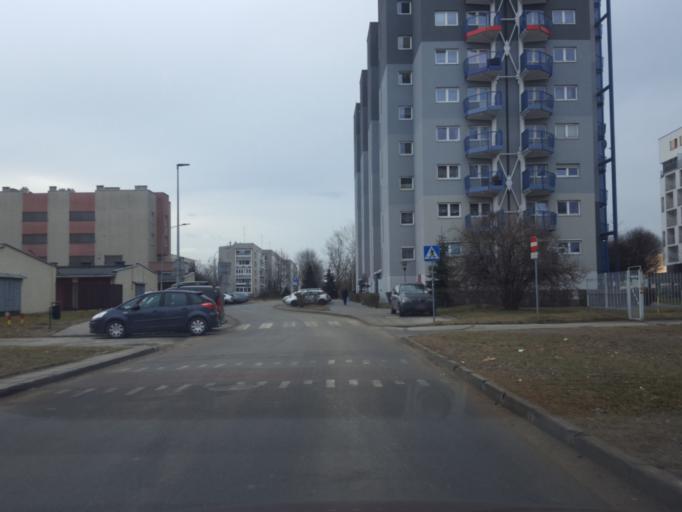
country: PL
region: Lesser Poland Voivodeship
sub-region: Krakow
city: Krakow
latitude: 50.0805
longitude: 20.0132
